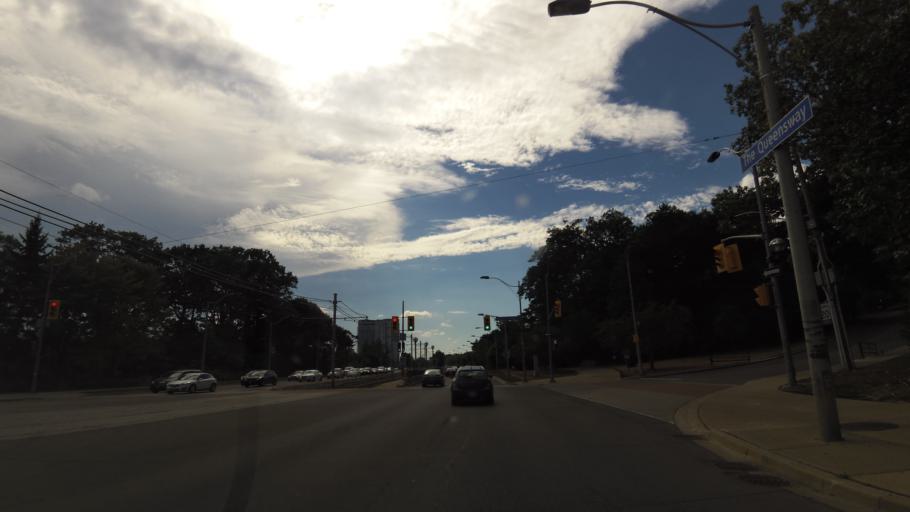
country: CA
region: Ontario
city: Toronto
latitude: 43.6396
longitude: -79.4592
